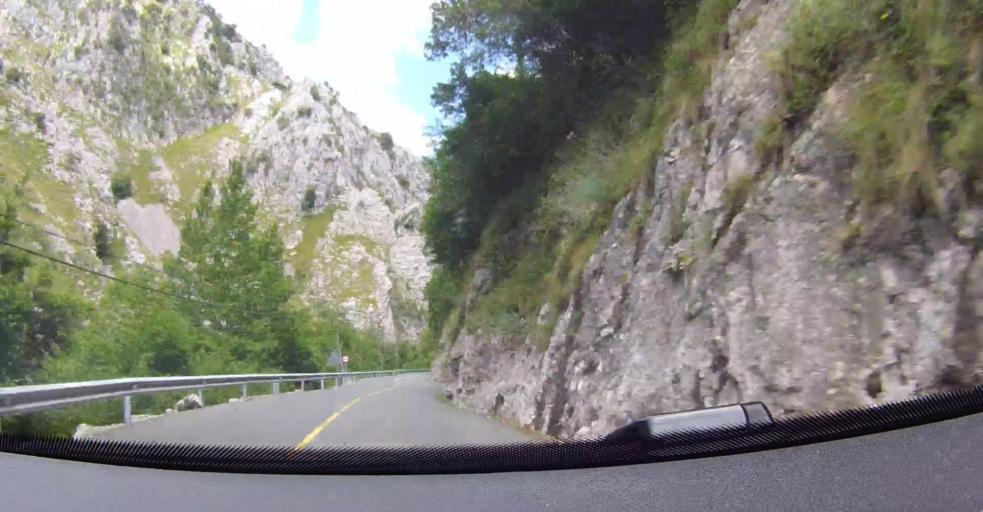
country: ES
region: Cantabria
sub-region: Provincia de Cantabria
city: Tresviso
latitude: 43.3006
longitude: -4.6063
